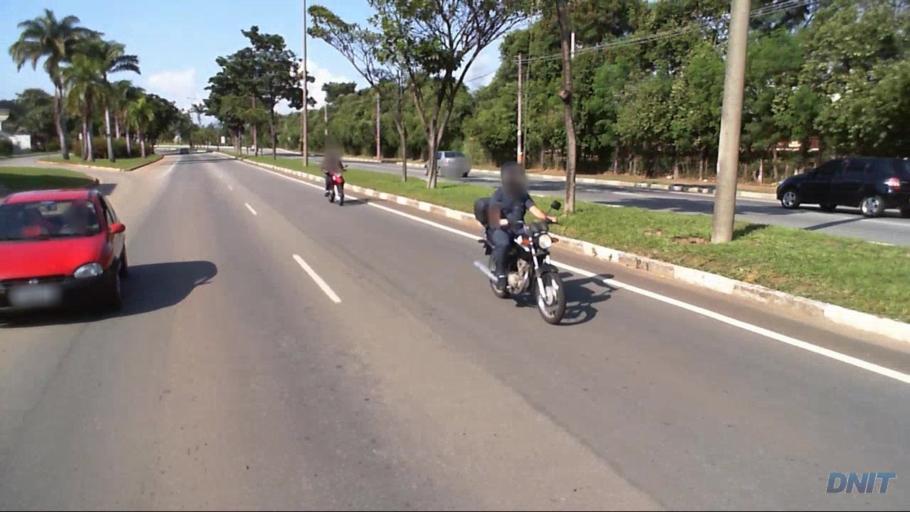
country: BR
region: Minas Gerais
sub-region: Ipatinga
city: Ipatinga
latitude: -19.4824
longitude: -42.5478
